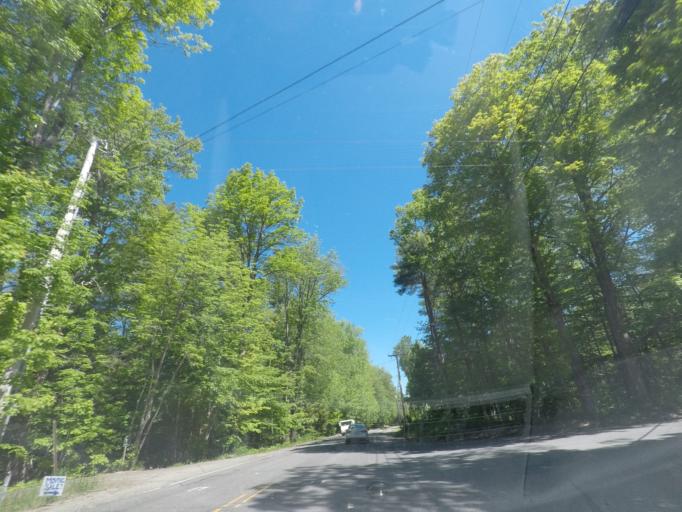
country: US
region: Maine
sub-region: Kennebec County
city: Manchester
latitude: 44.2924
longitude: -69.8890
